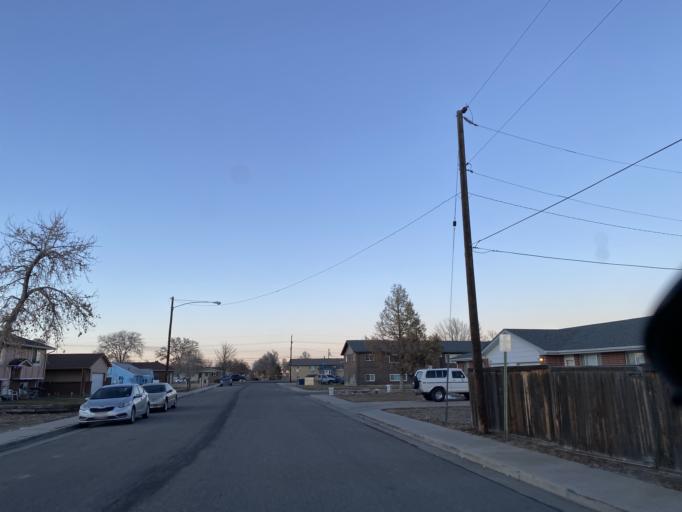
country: US
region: Colorado
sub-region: Adams County
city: Brighton
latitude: 39.9762
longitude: -104.8154
